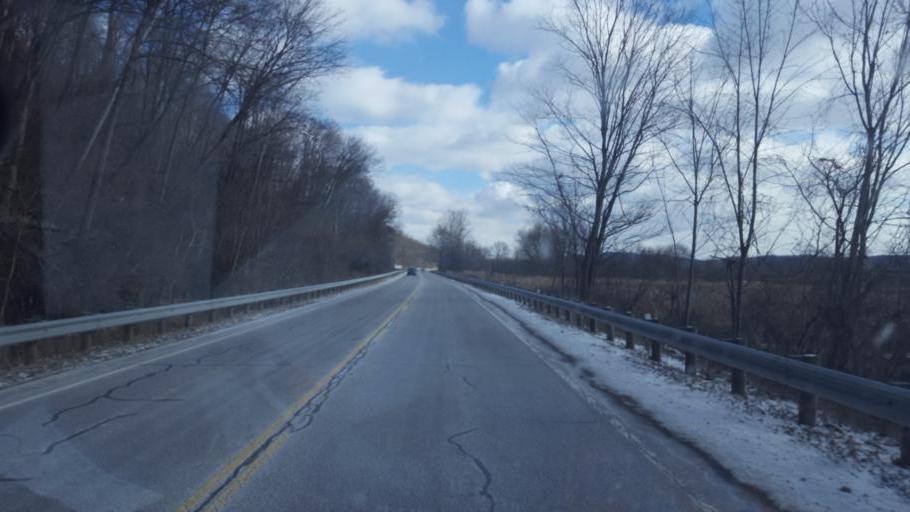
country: US
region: Ohio
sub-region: Muskingum County
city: Dresden
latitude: 40.1544
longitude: -81.9626
